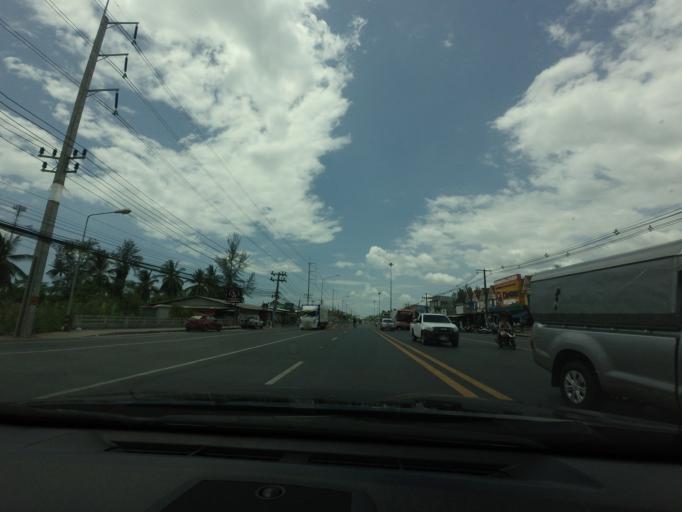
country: TH
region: Phangnga
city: Ban Khao Lak
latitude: 8.6653
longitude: 98.2531
